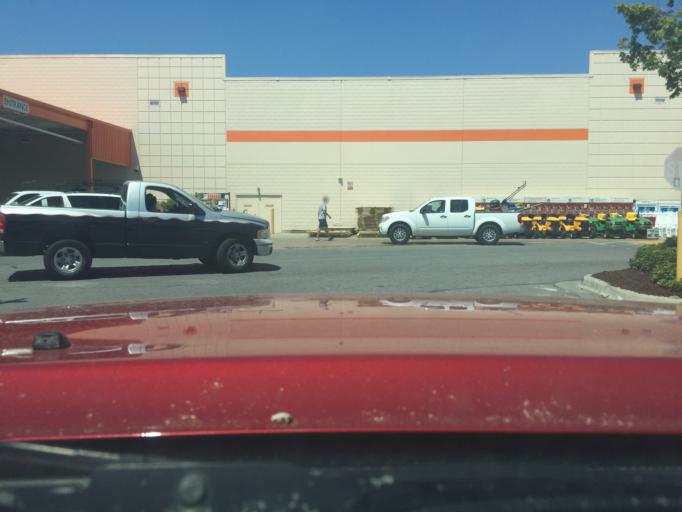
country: US
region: Georgia
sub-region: Chatham County
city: Thunderbolt
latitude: 32.0417
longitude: -81.0677
